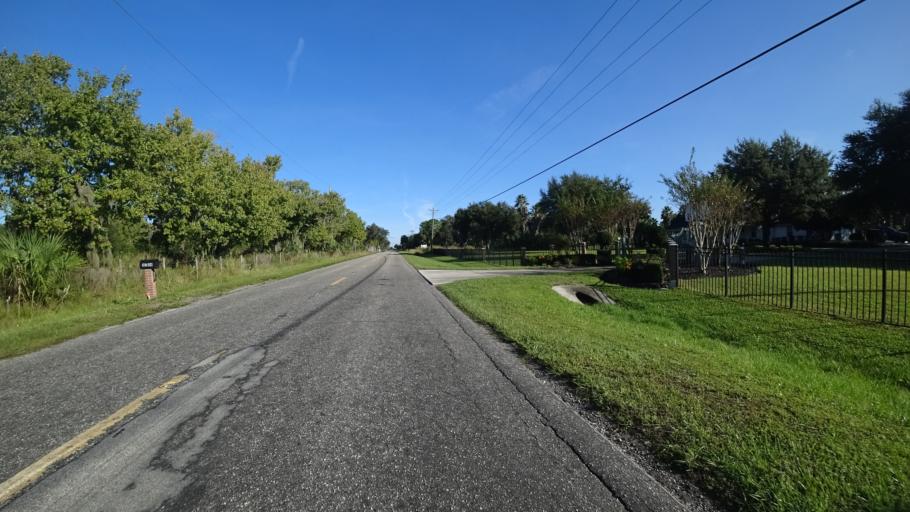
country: US
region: Florida
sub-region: Manatee County
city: Memphis
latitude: 27.5904
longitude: -82.5273
